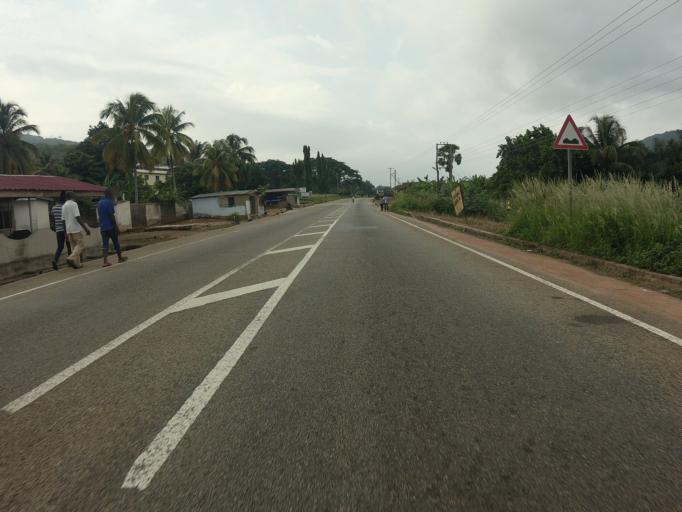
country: GH
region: Volta
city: Ho
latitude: 6.6598
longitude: 0.4717
